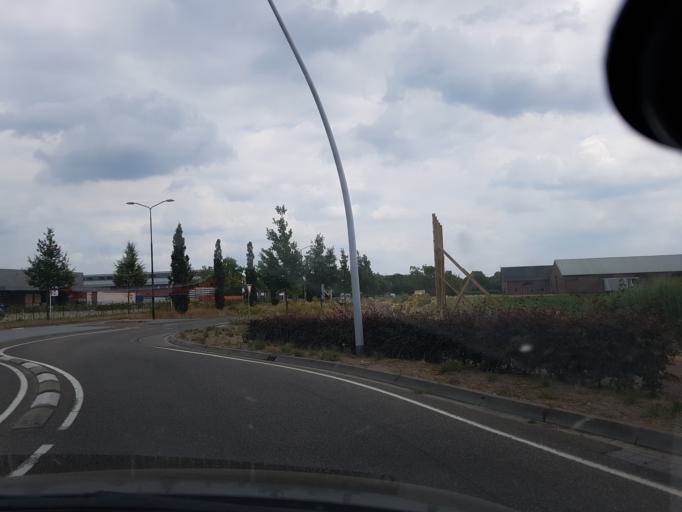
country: NL
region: North Brabant
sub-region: Gemeente Geldrop-Mierlo
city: Geldrop
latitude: 51.4445
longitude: 5.5560
